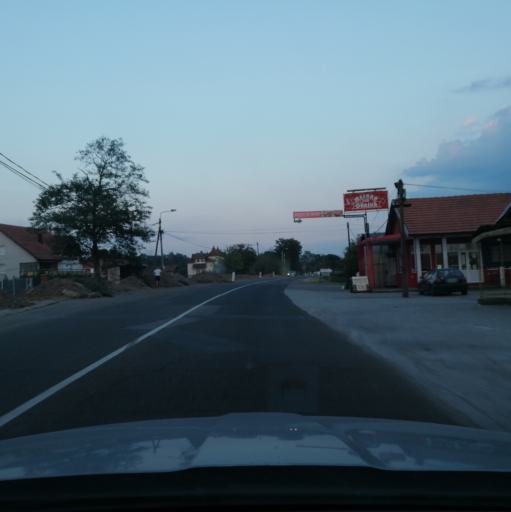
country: RS
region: Central Serbia
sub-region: Raski Okrug
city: Kraljevo
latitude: 43.7030
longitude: 20.7273
